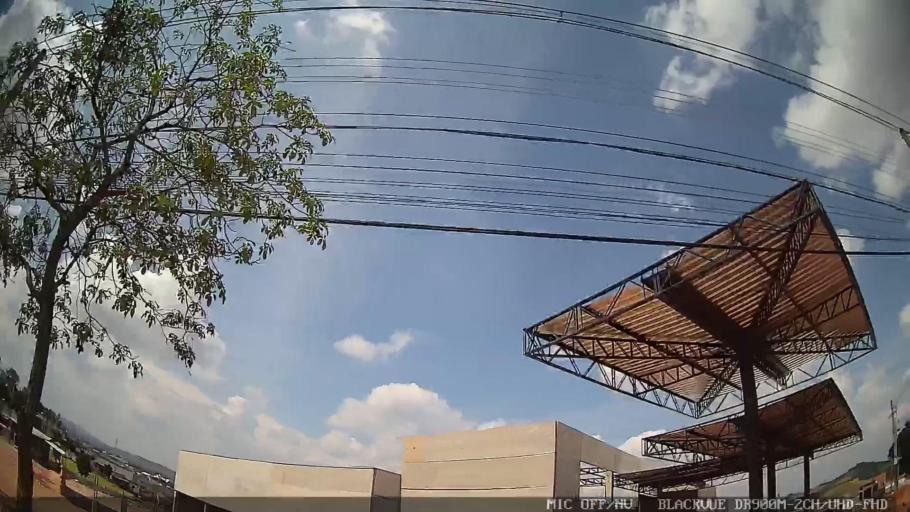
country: BR
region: Sao Paulo
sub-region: Itatiba
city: Itatiba
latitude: -23.0141
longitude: -46.8193
